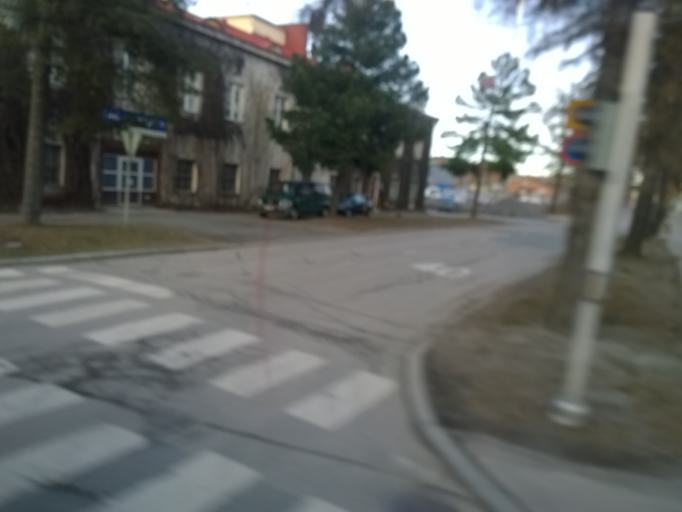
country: FI
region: Pirkanmaa
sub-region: Tampere
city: Tampere
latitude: 61.4837
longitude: 23.7626
